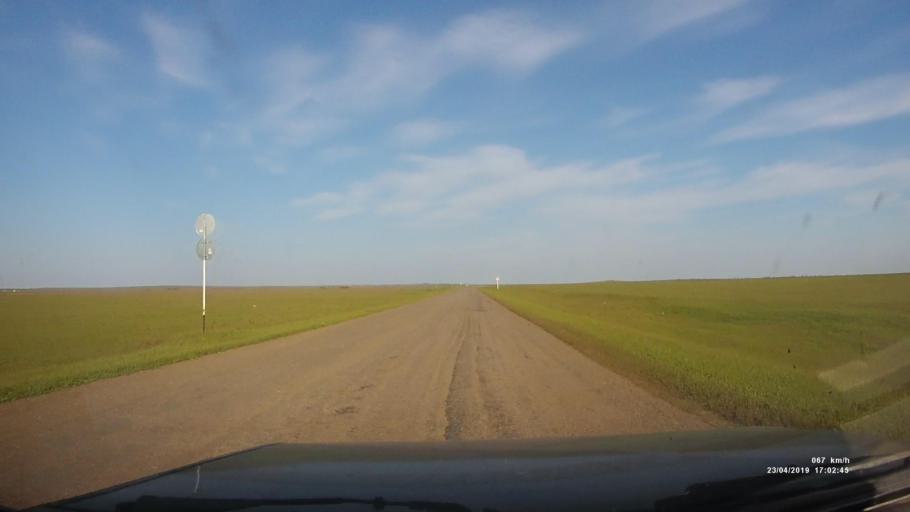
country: RU
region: Kalmykiya
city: Priyutnoye
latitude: 46.2917
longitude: 43.4219
